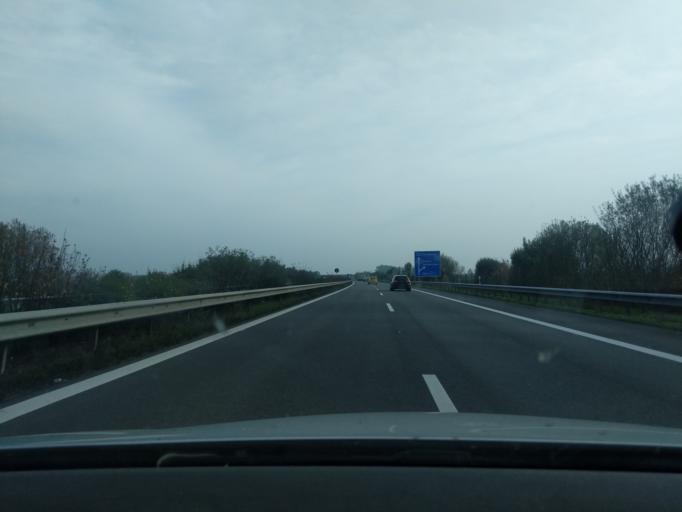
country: DE
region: Lower Saxony
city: Dollern
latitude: 53.5505
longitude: 9.5639
